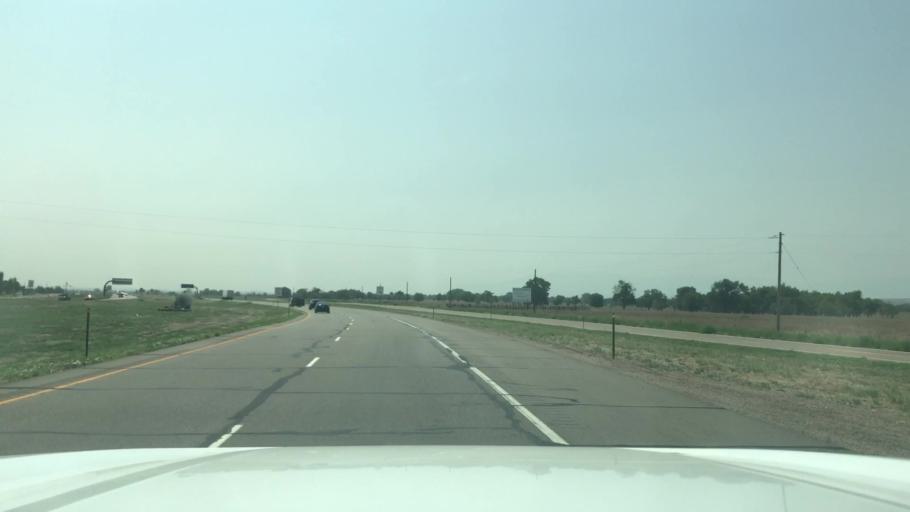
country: US
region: Colorado
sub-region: Pueblo County
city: Pueblo
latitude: 38.2124
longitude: -104.6270
